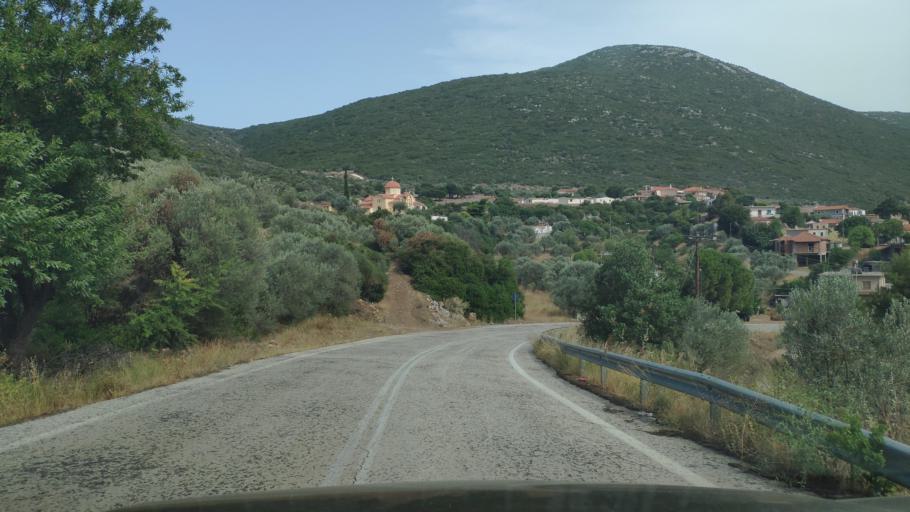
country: GR
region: Peloponnese
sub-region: Nomos Argolidos
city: Palaia Epidavros
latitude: 37.5959
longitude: 23.1585
